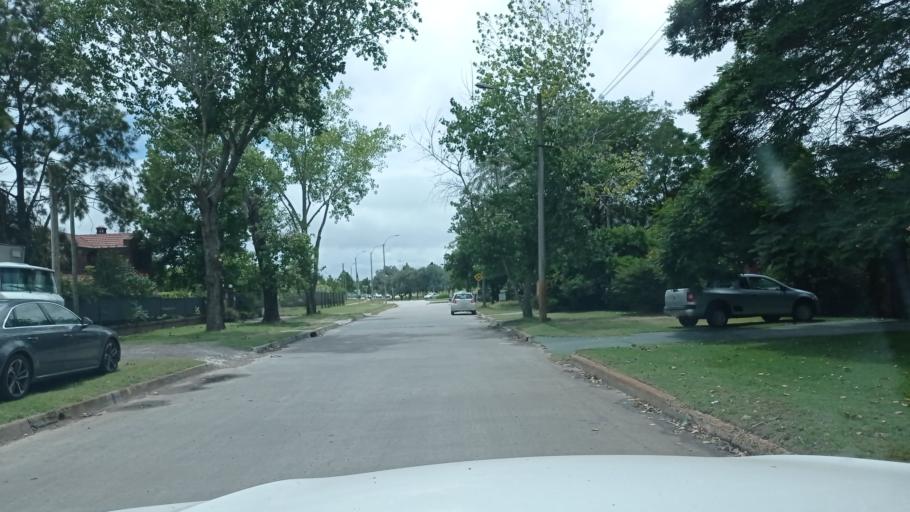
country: UY
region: Canelones
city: Barra de Carrasco
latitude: -34.8781
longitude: -56.0386
